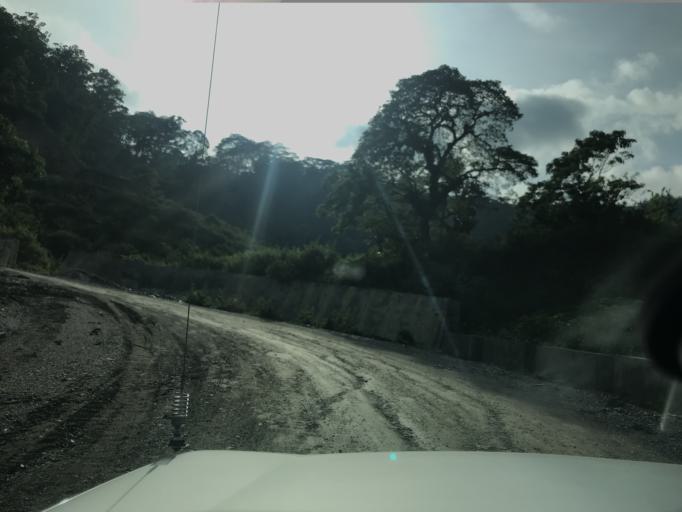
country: TL
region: Aileu
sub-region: Aileu Villa
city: Aileu
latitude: -8.6661
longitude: 125.5503
